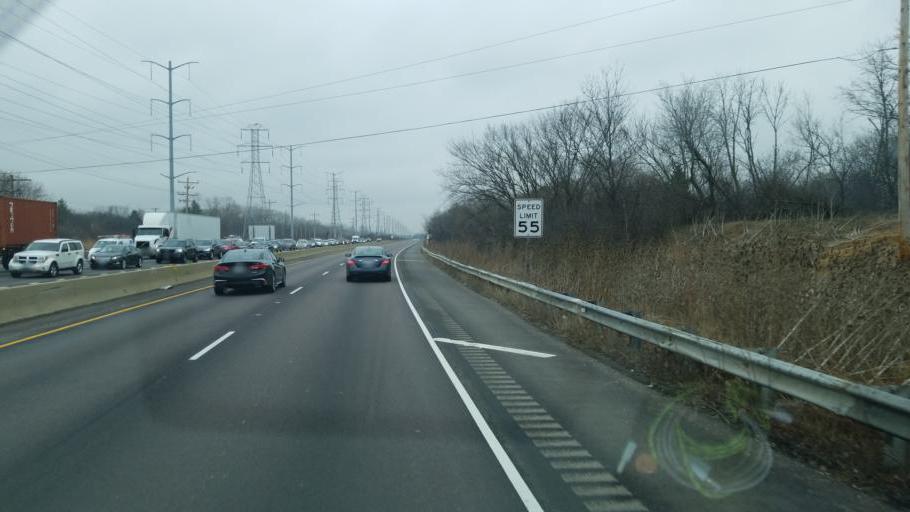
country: US
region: Illinois
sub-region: Lake County
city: Bannockburn
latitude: 42.2184
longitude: -87.8457
